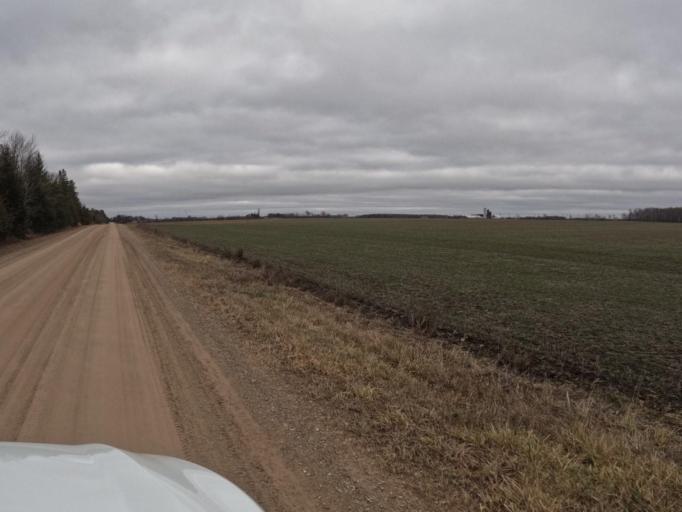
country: CA
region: Ontario
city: Shelburne
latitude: 43.9466
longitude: -80.3959
